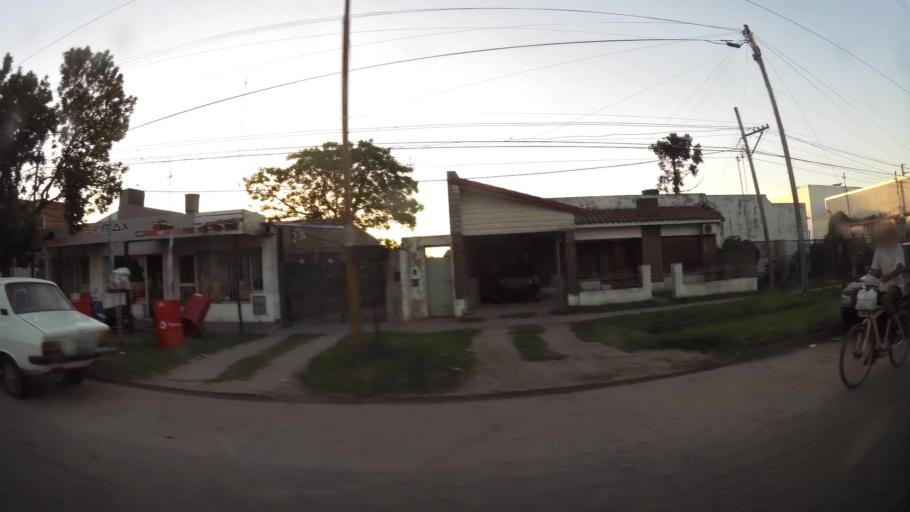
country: AR
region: Santa Fe
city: Santa Fe de la Vera Cruz
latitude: -31.5915
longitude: -60.6922
